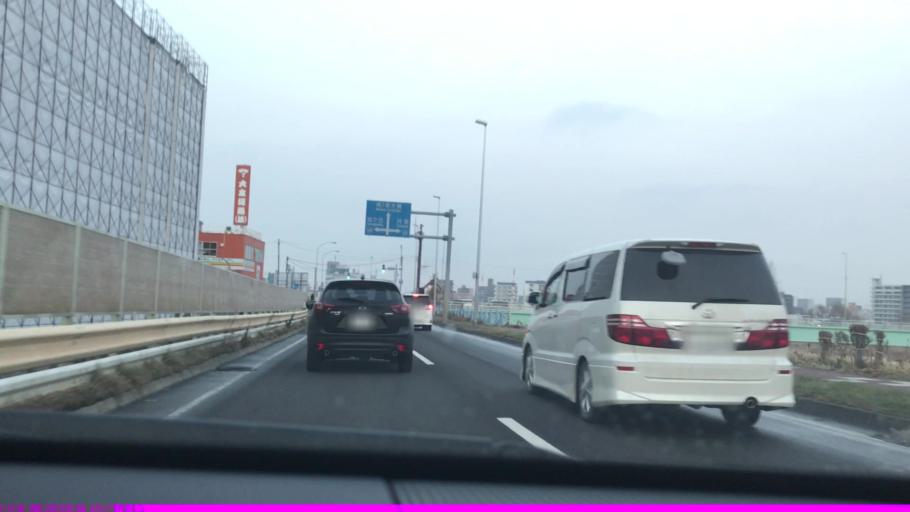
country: JP
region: Hokkaido
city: Sapporo
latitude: 43.0292
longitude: 141.3530
